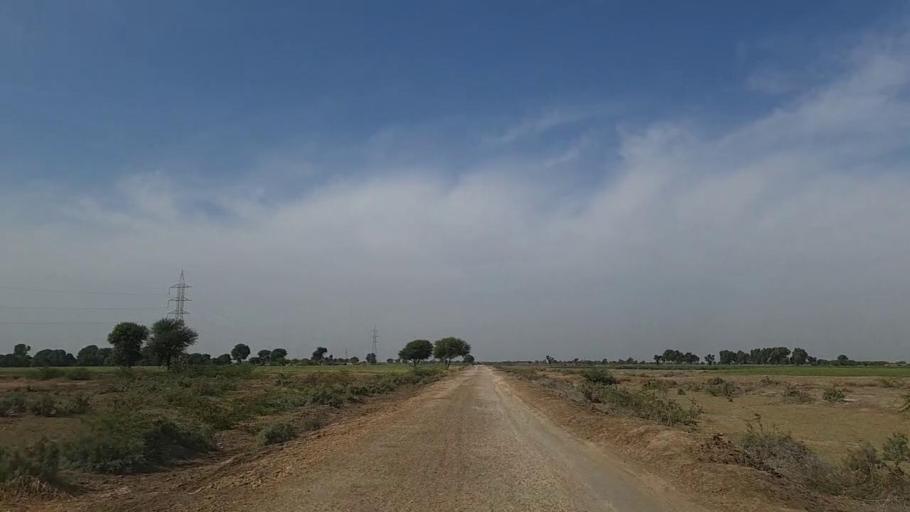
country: PK
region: Sindh
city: Samaro
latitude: 25.2150
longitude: 69.4533
